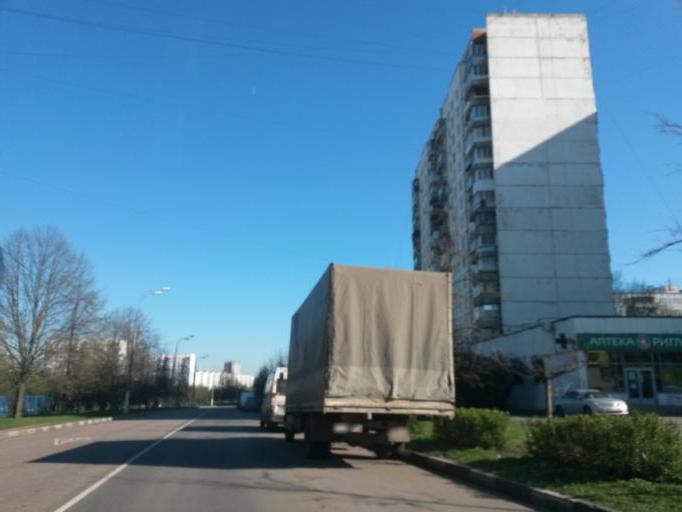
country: RU
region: Moscow
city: Orekhovo-Borisovo
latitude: 55.6157
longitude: 37.7304
